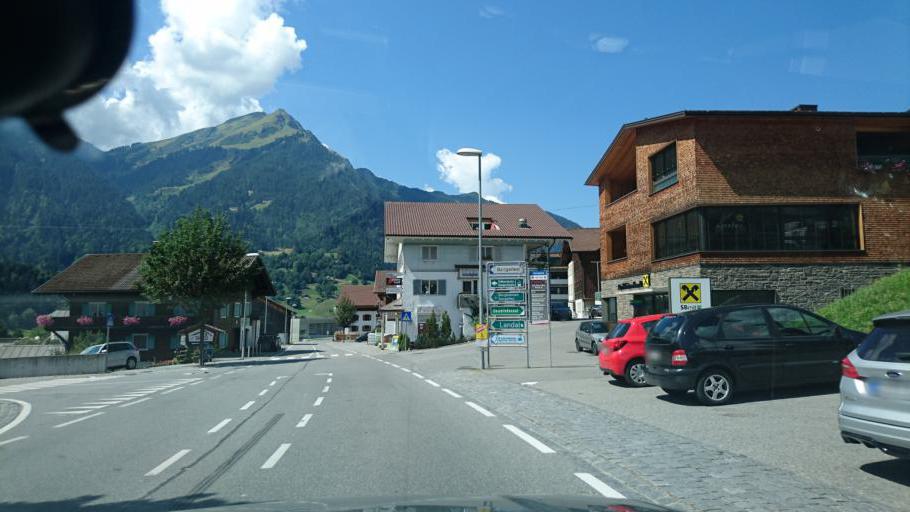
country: AT
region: Vorarlberg
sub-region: Politischer Bezirk Bludenz
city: Sankt Gallenkirch
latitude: 47.0210
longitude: 9.9730
